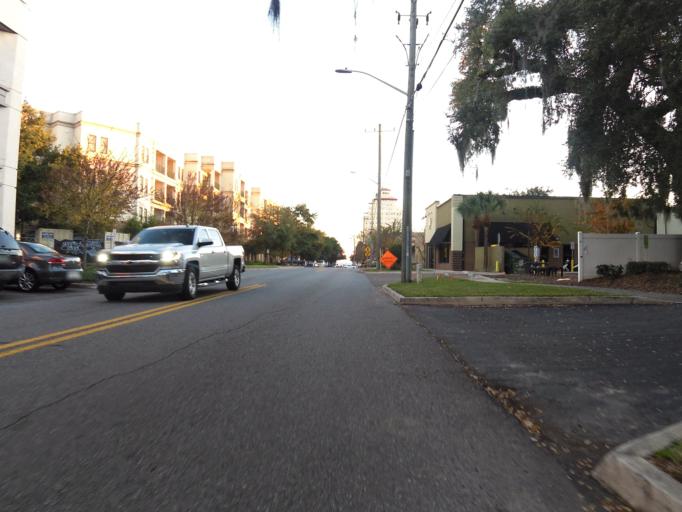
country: US
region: Florida
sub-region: Duval County
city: Jacksonville
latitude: 30.3127
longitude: -81.6811
